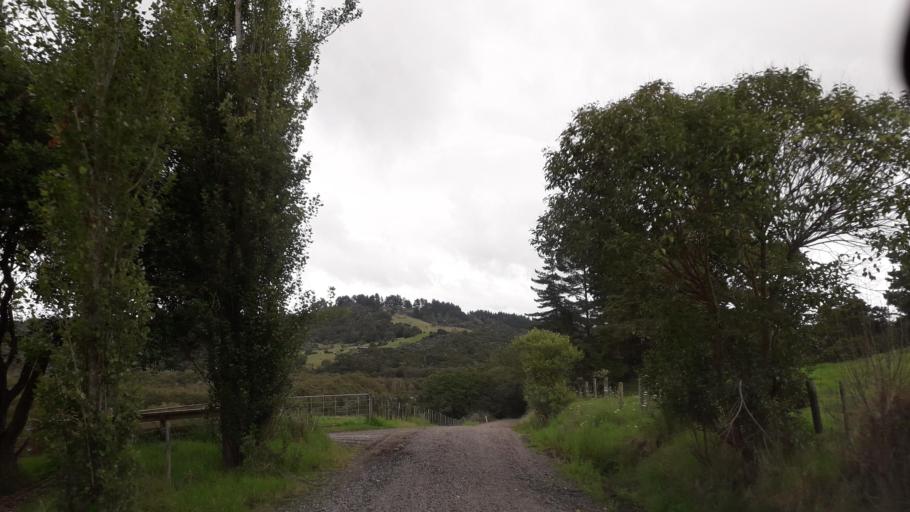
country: NZ
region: Northland
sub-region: Far North District
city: Waimate North
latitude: -35.3163
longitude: 173.5711
